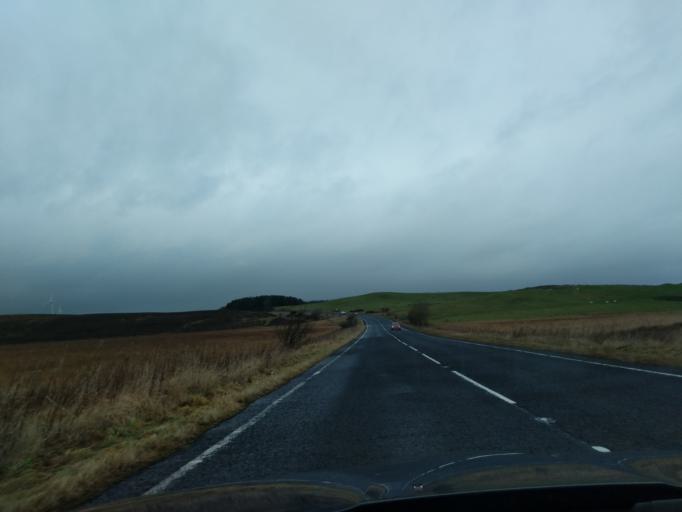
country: GB
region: England
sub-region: Northumberland
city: Rothley
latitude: 55.1720
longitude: -2.0249
